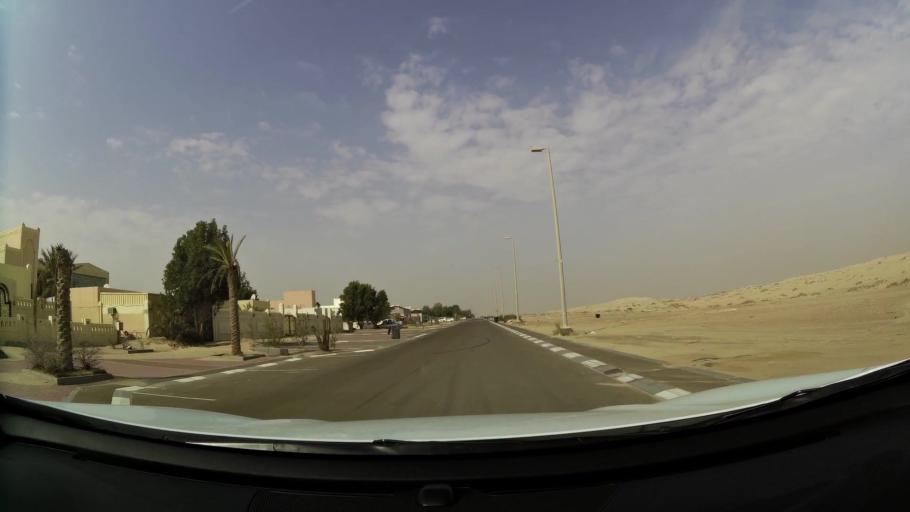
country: AE
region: Abu Dhabi
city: Abu Dhabi
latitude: 24.2802
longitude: 54.6943
